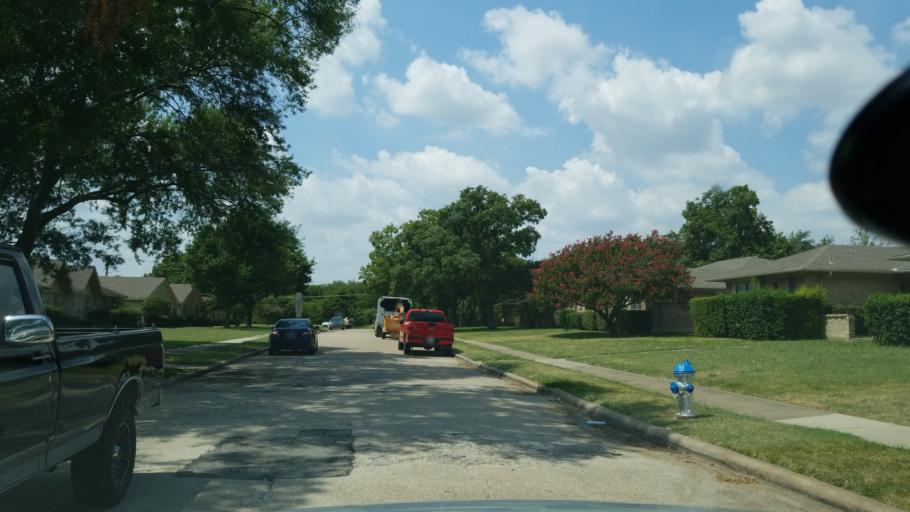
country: US
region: Texas
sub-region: Dallas County
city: Richardson
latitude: 32.9297
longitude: -96.7330
